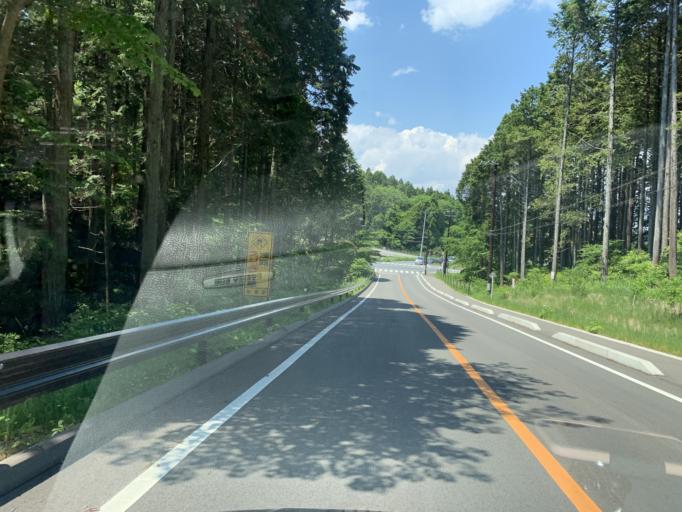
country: JP
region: Miyagi
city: Matsushima
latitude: 38.3693
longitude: 141.0515
